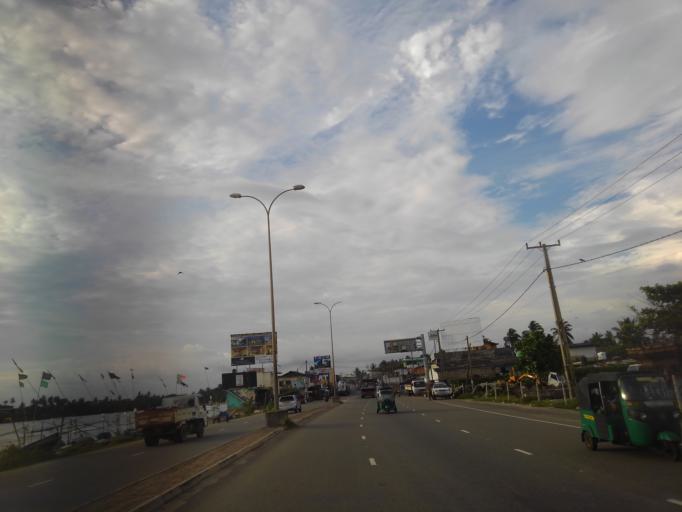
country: LK
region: Southern
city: Unawatuna
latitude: 6.0301
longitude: 80.2414
